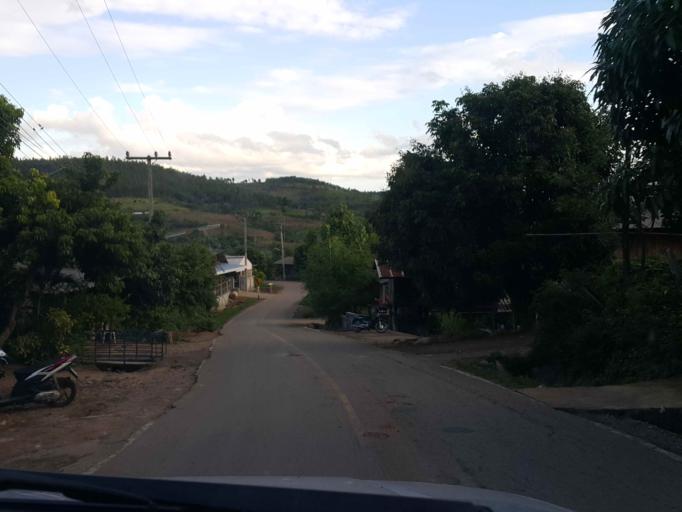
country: TH
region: Chiang Mai
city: Mae Chaem
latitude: 18.5219
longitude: 98.3975
